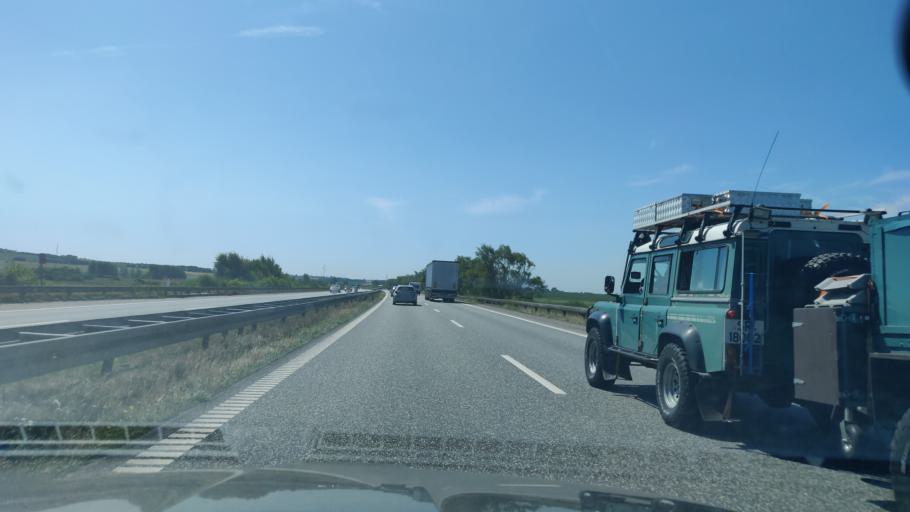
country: DK
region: North Denmark
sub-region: Rebild Kommune
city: Stovring
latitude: 56.8189
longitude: 9.7182
